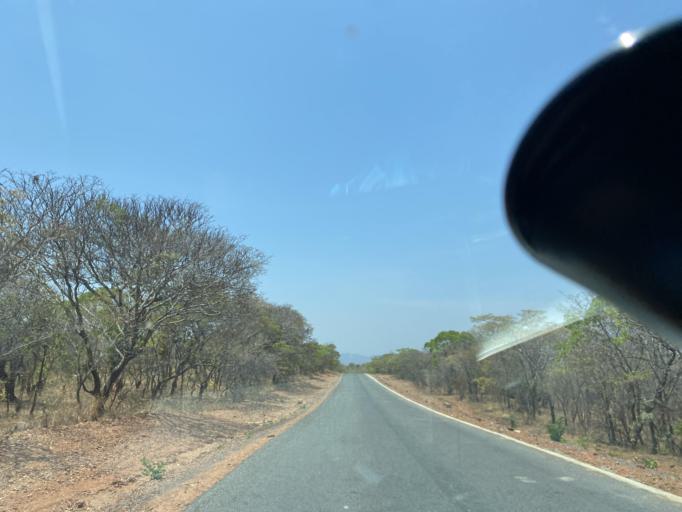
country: ZM
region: Lusaka
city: Kafue
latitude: -15.8611
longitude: 28.4256
